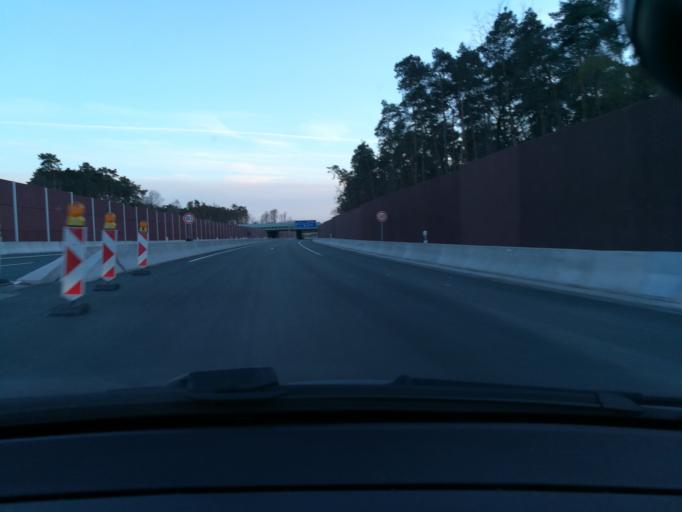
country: DE
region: North Rhine-Westphalia
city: Halle
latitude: 52.0516
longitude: 8.3405
